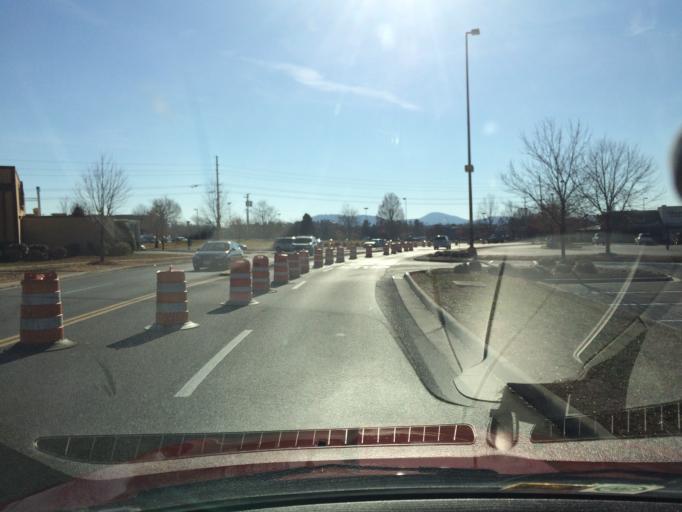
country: US
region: Virginia
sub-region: City of Roanoke
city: Roanoke
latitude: 37.3044
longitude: -79.9607
